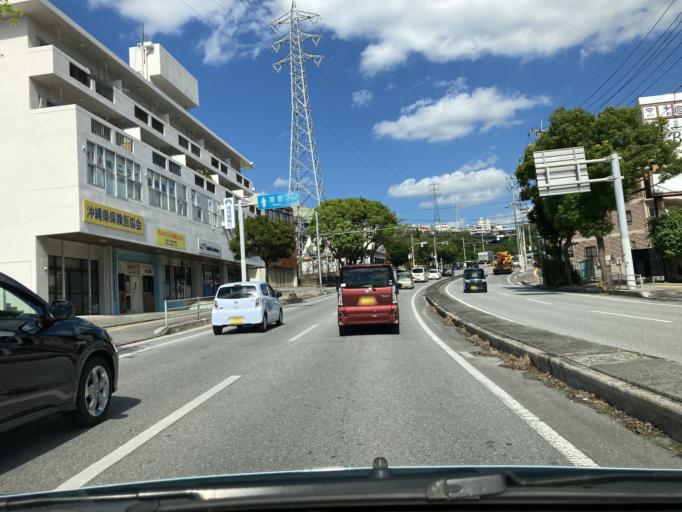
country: JP
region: Okinawa
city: Naha-shi
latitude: 26.2002
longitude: 127.7145
